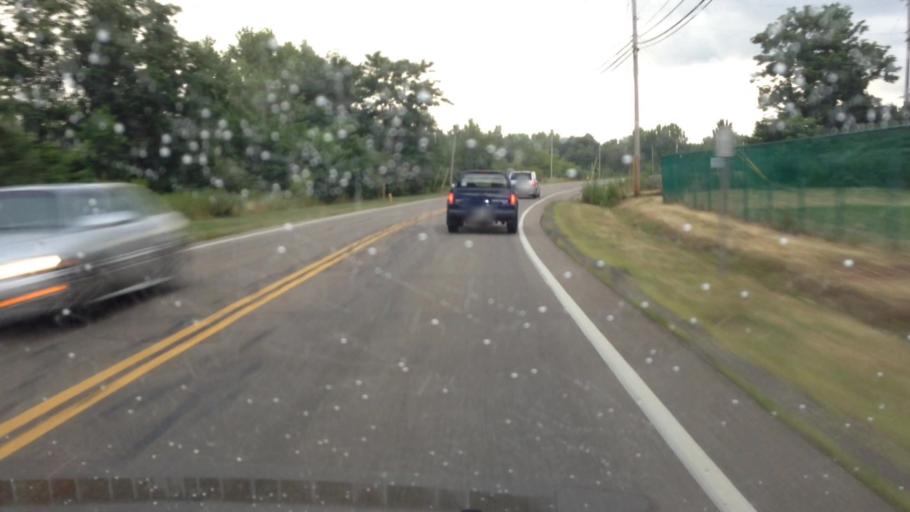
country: US
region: Ohio
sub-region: Summit County
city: Portage Lakes
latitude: 41.0153
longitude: -81.5328
